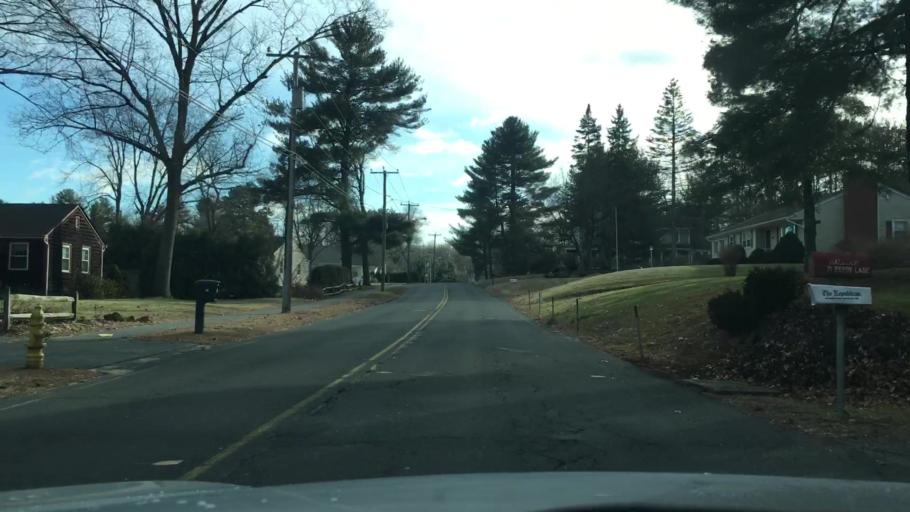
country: US
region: Massachusetts
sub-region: Hampden County
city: Agawam
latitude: 42.0659
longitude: -72.6283
